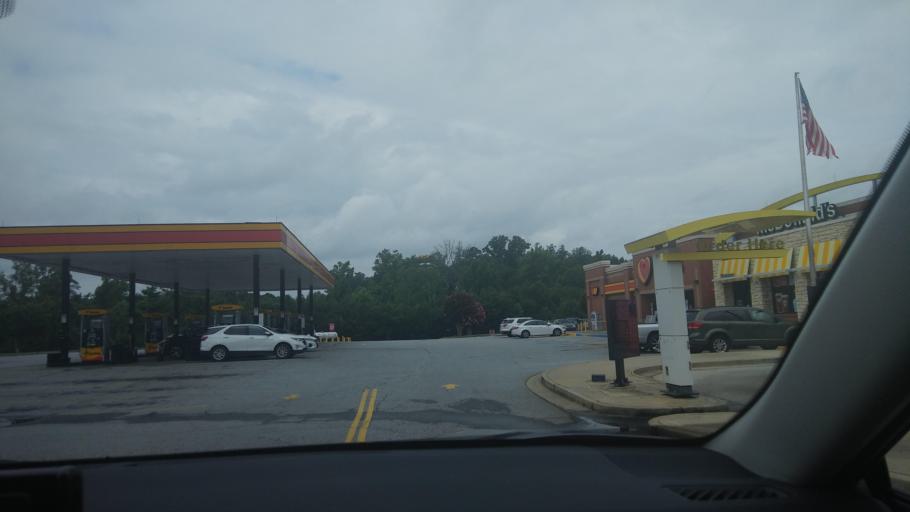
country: US
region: South Carolina
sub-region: Newberry County
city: Newberry
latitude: 34.2961
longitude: -81.5435
